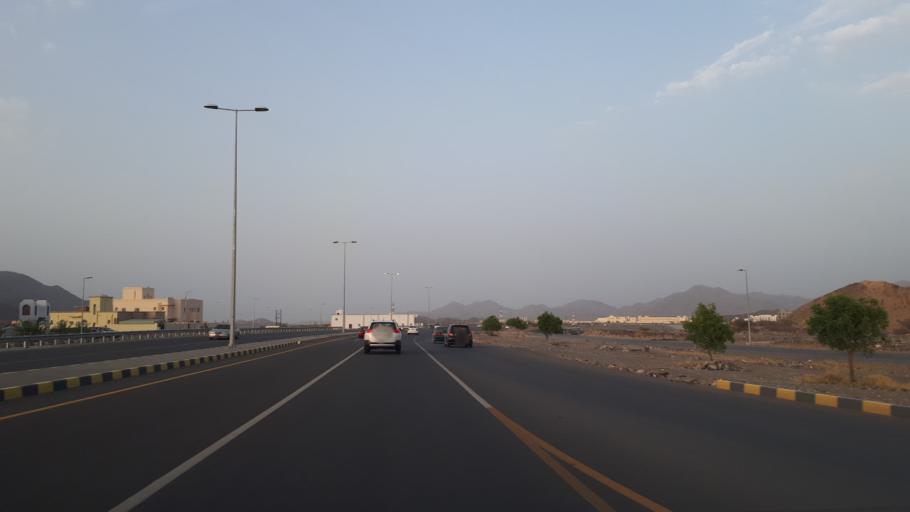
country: OM
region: Al Batinah
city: Rustaq
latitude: 23.4383
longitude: 57.3978
